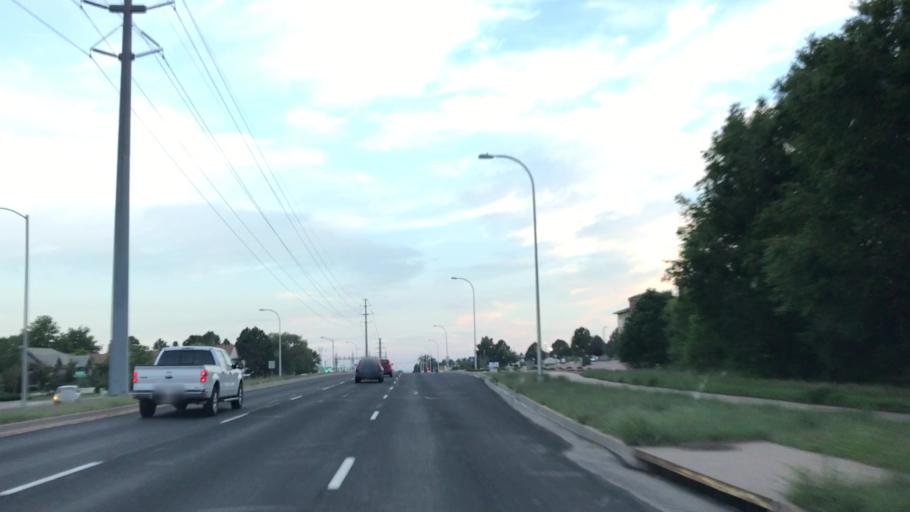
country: US
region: Colorado
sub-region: El Paso County
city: Cimarron Hills
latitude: 38.8636
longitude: -104.7573
